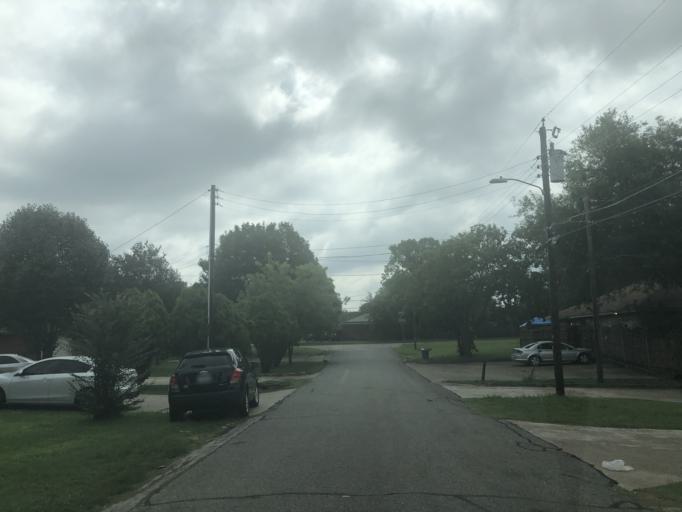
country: US
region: Texas
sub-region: Dallas County
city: Irving
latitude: 32.8066
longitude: -96.9639
